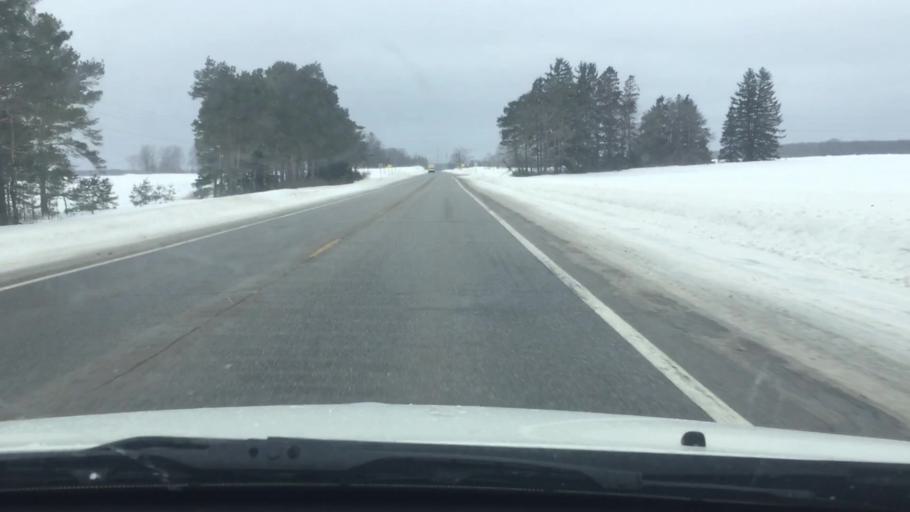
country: US
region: Michigan
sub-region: Otsego County
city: Gaylord
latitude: 45.0664
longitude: -84.8752
